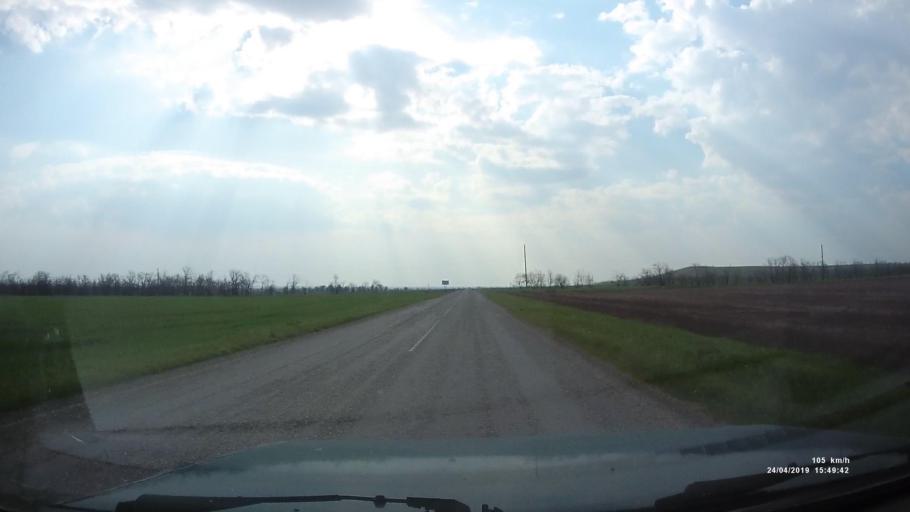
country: RU
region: Kalmykiya
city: Yashalta
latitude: 46.6038
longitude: 42.6495
